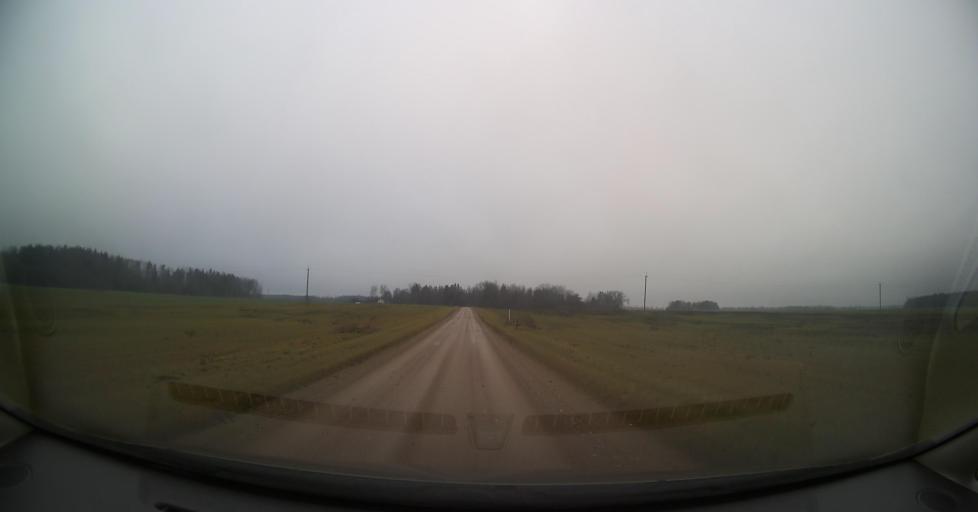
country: EE
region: Tartu
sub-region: Tartu linn
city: Tartu
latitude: 58.3749
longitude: 26.9312
